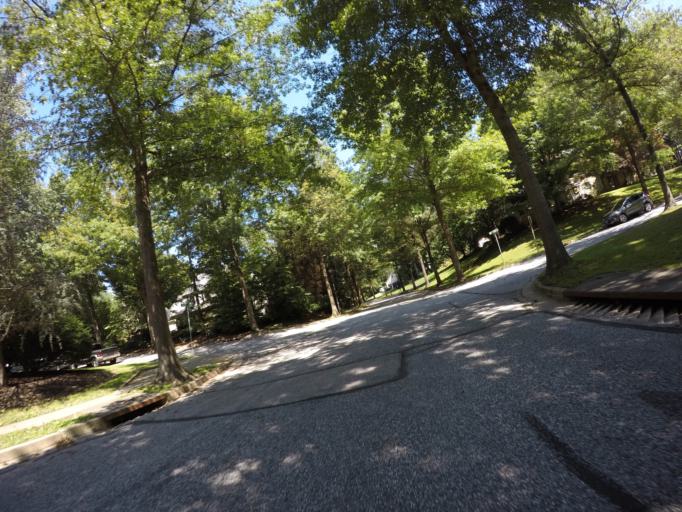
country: US
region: Maryland
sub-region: Howard County
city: Columbia
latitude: 39.2871
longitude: -76.8798
